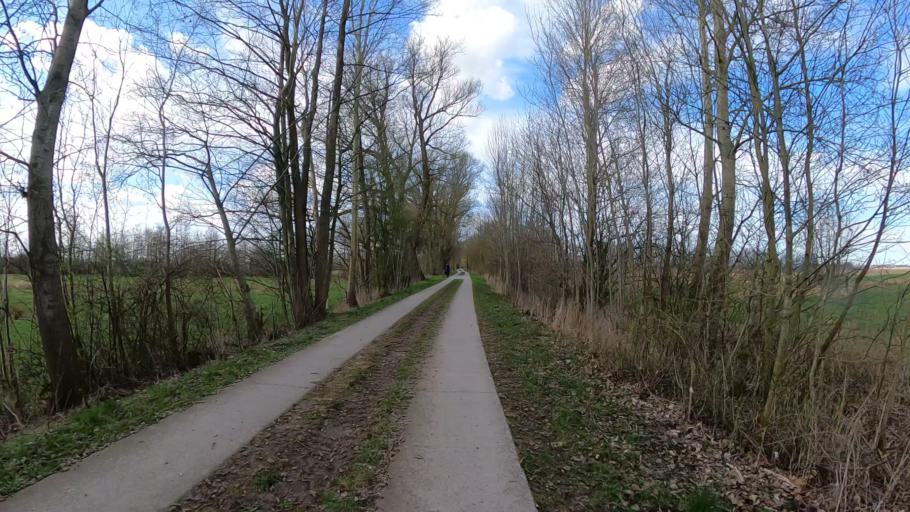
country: DE
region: Lower Saxony
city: Stelle
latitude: 53.4204
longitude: 10.1725
